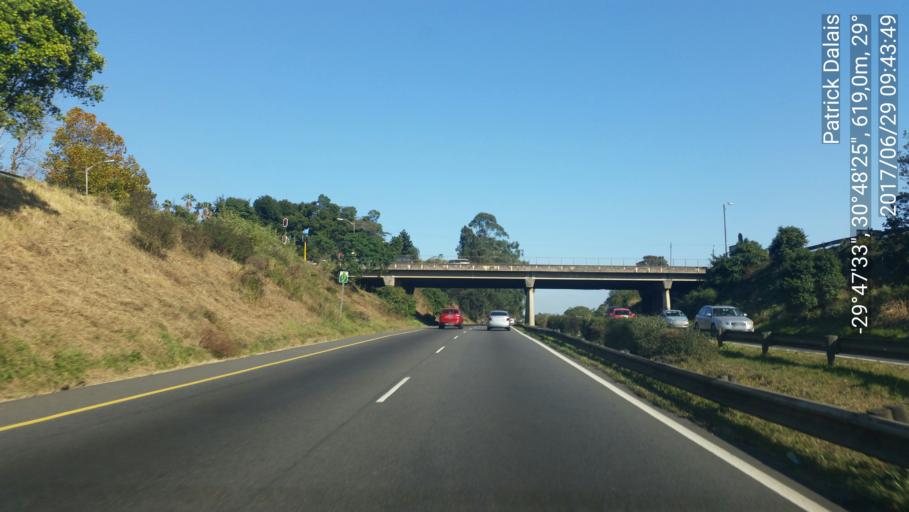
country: ZA
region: KwaZulu-Natal
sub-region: eThekwini Metropolitan Municipality
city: Mpumalanga
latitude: -29.7925
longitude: 30.8073
